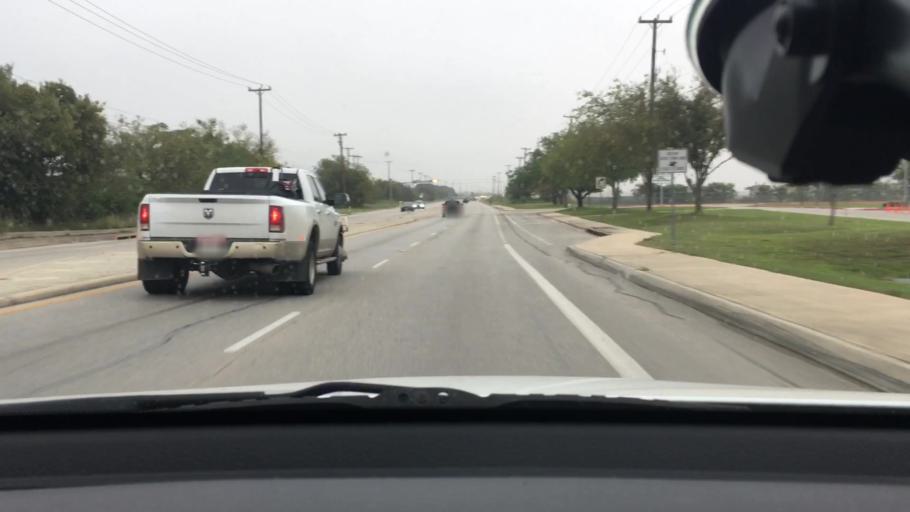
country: US
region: Texas
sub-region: Bexar County
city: Live Oak
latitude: 29.5960
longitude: -98.3434
